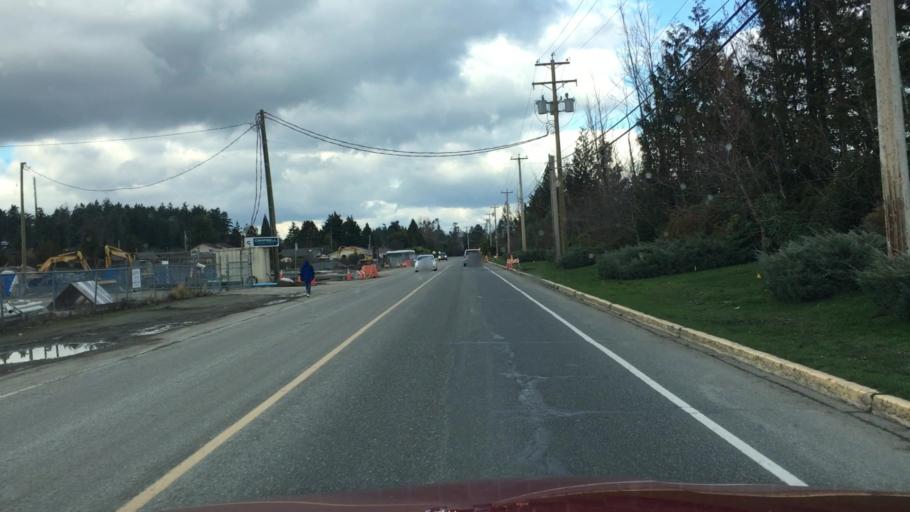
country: CA
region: British Columbia
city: North Saanich
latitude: 48.5962
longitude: -123.3946
